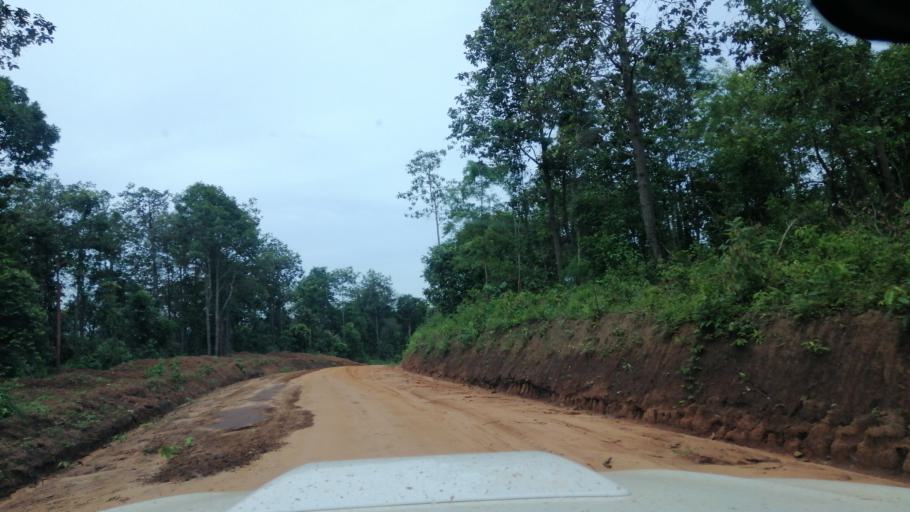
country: TH
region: Loei
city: Na Haeo
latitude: 17.5777
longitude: 101.1664
